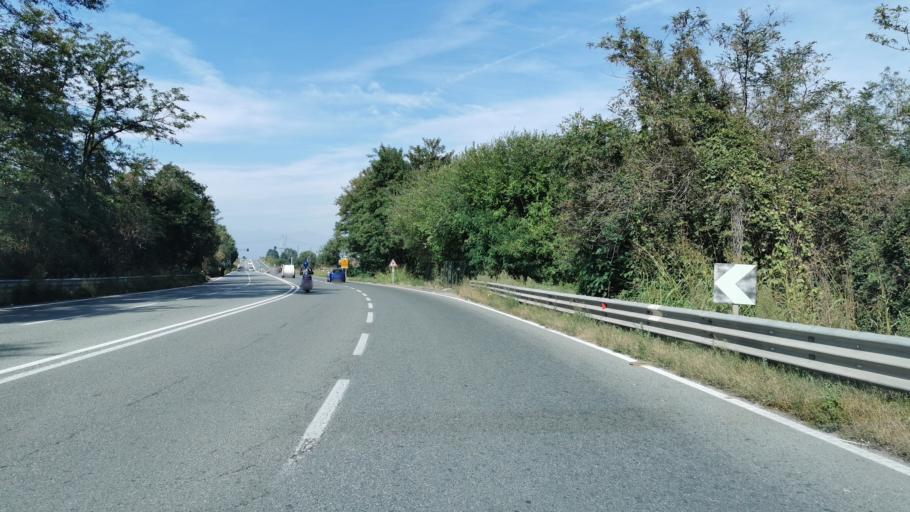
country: IT
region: Piedmont
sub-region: Provincia di Torino
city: Venaria Reale
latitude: 45.1211
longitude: 7.6614
